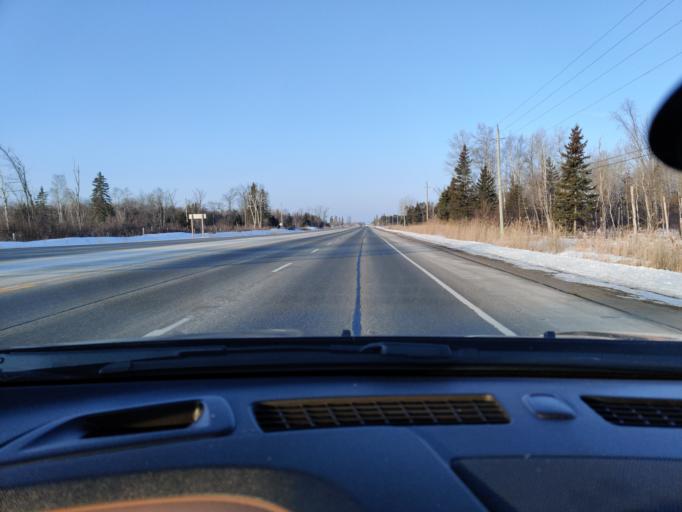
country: CA
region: Ontario
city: Barrie
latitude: 44.3602
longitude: -79.7506
